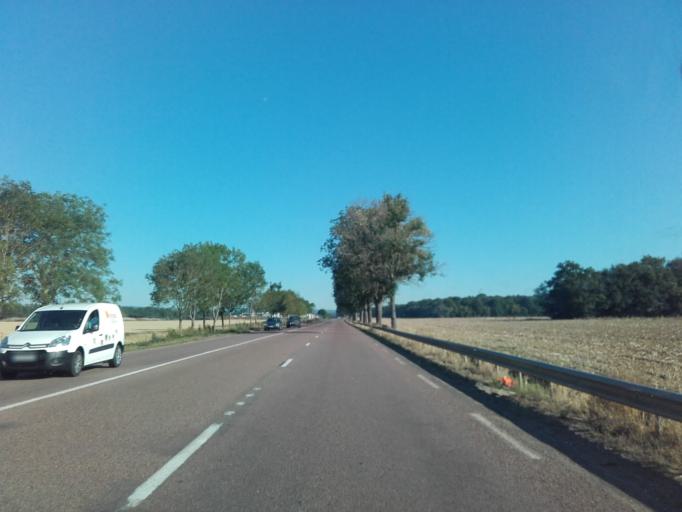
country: FR
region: Bourgogne
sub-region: Departement de Saone-et-Loire
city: Fontaines
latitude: 46.8494
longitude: 4.8077
